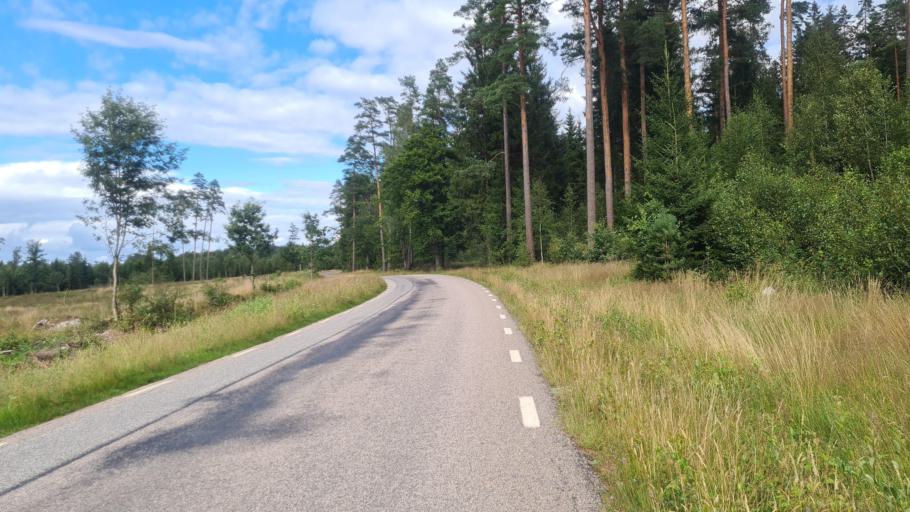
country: SE
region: Kronoberg
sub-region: Ljungby Kommun
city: Ljungby
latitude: 56.8099
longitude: 13.8337
